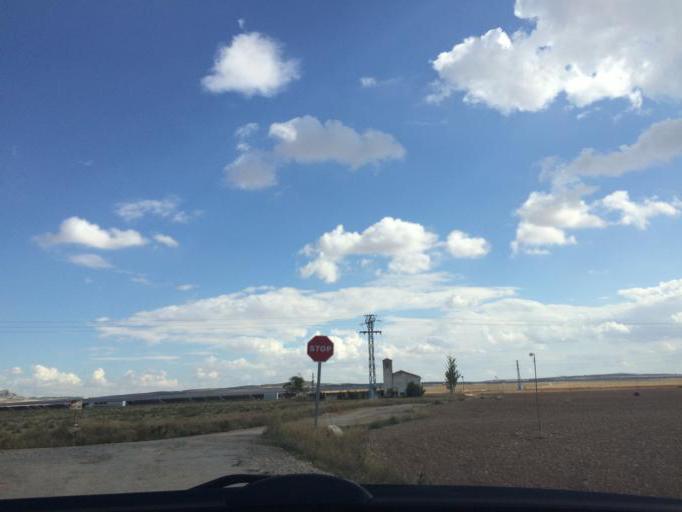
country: ES
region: Castille-La Mancha
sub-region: Provincia de Albacete
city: Albacete
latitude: 38.9465
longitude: -1.8273
